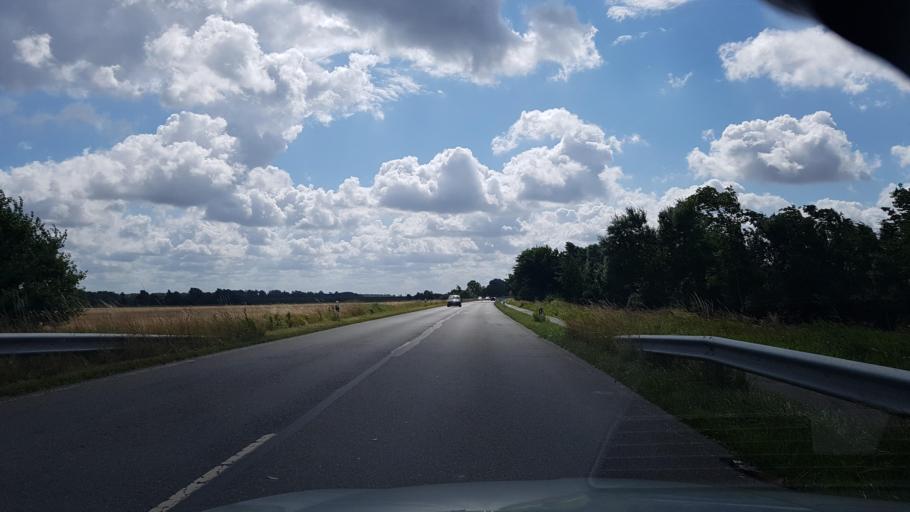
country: DE
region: Schleswig-Holstein
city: Vollerwiek
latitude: 54.2971
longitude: 8.8176
